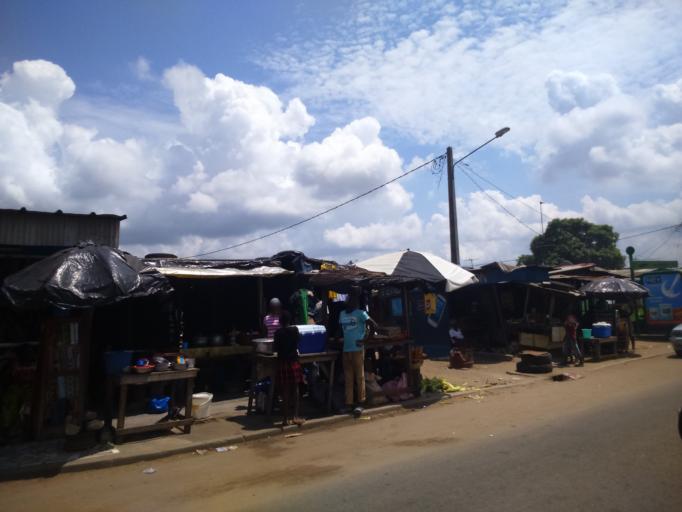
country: CI
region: Lagunes
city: Abidjan
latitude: 5.3479
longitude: -4.0875
